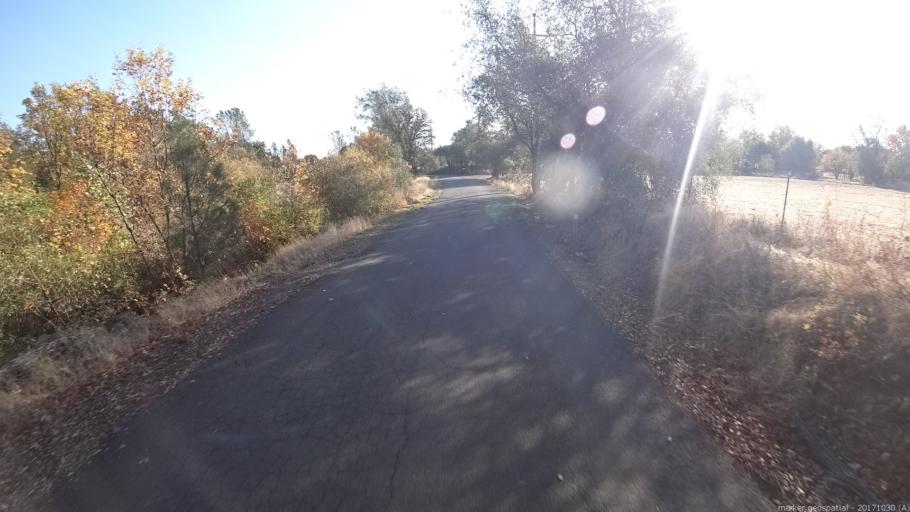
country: US
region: California
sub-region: Shasta County
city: Palo Cedro
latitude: 40.5636
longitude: -122.1981
